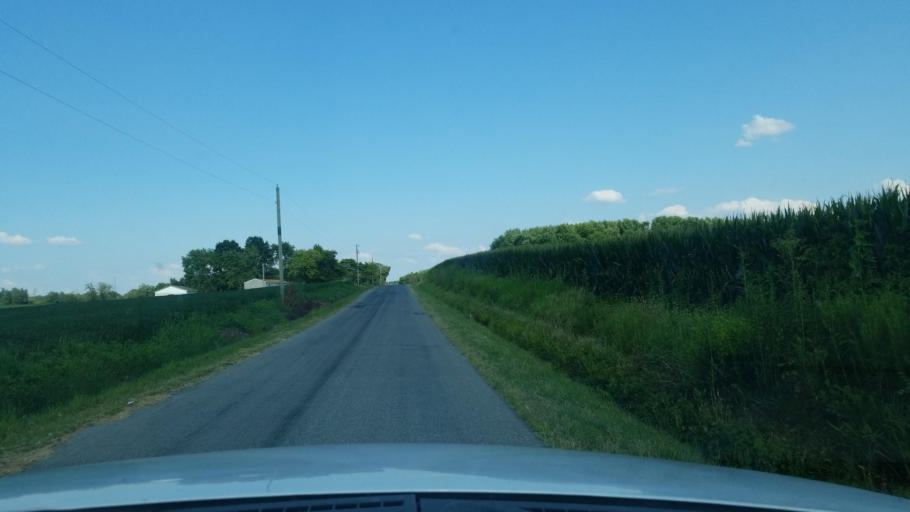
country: US
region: Illinois
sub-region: Saline County
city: Eldorado
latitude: 37.8048
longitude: -88.4733
